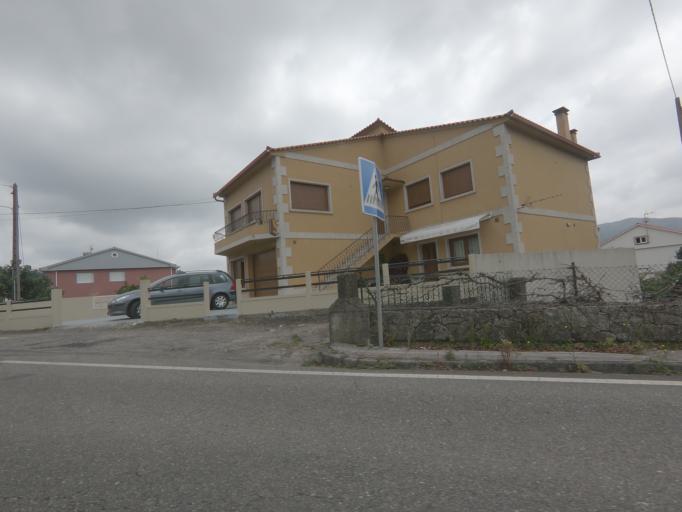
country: ES
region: Galicia
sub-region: Provincia de Pontevedra
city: O Rosal
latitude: 41.9260
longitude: -8.8050
